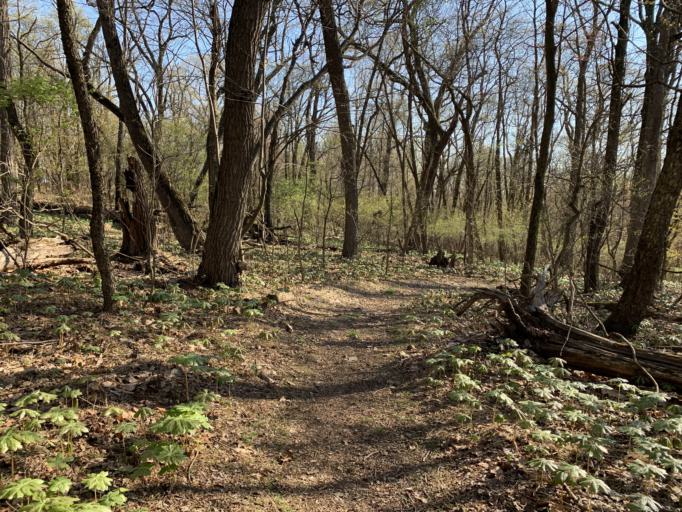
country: US
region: Pennsylvania
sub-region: Berks County
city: Mount Penn
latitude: 40.3204
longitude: -75.9112
